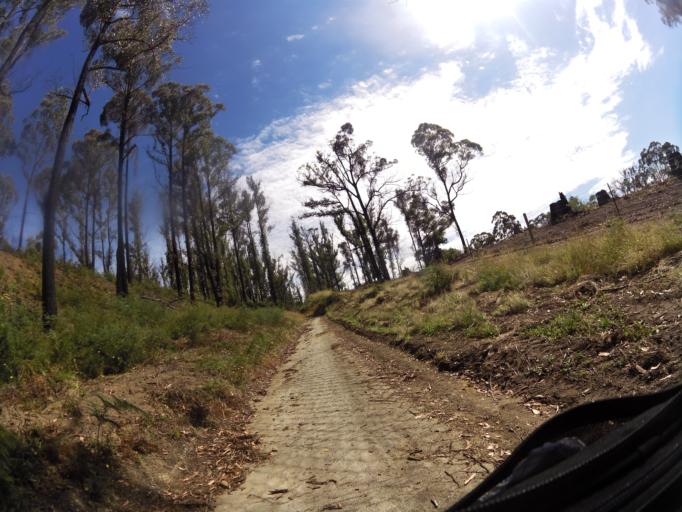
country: AU
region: Victoria
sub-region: East Gippsland
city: Lakes Entrance
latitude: -37.7315
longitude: 148.1624
